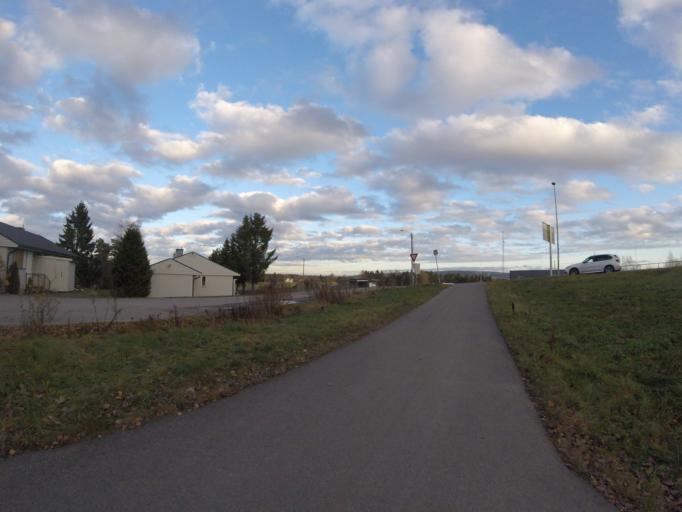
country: NO
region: Akershus
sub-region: Skedsmo
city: Lillestrom
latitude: 59.9973
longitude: 11.0441
